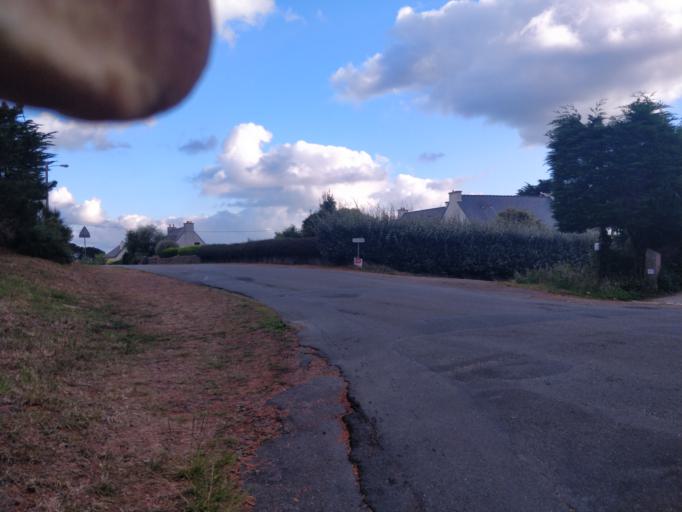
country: FR
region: Brittany
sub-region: Departement des Cotes-d'Armor
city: Tregastel
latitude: 48.8224
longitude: -3.4936
